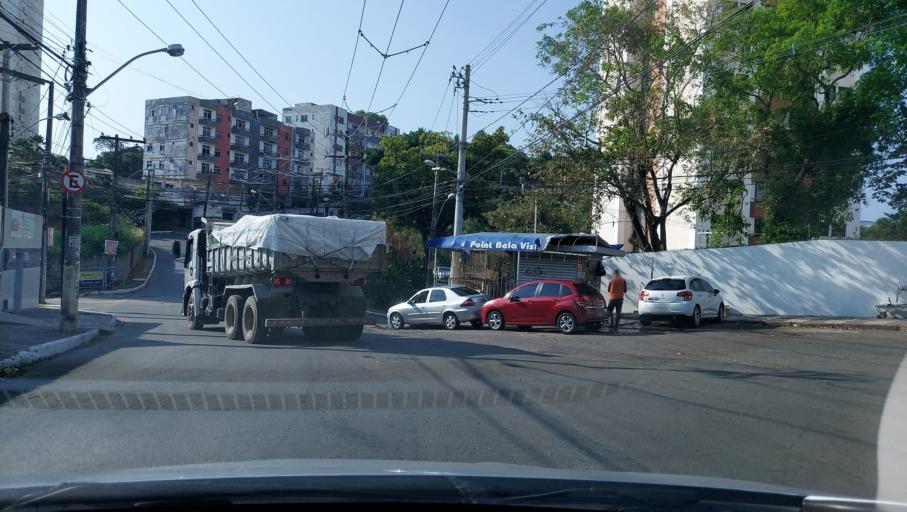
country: BR
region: Bahia
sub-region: Salvador
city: Salvador
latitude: -12.9862
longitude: -38.4697
